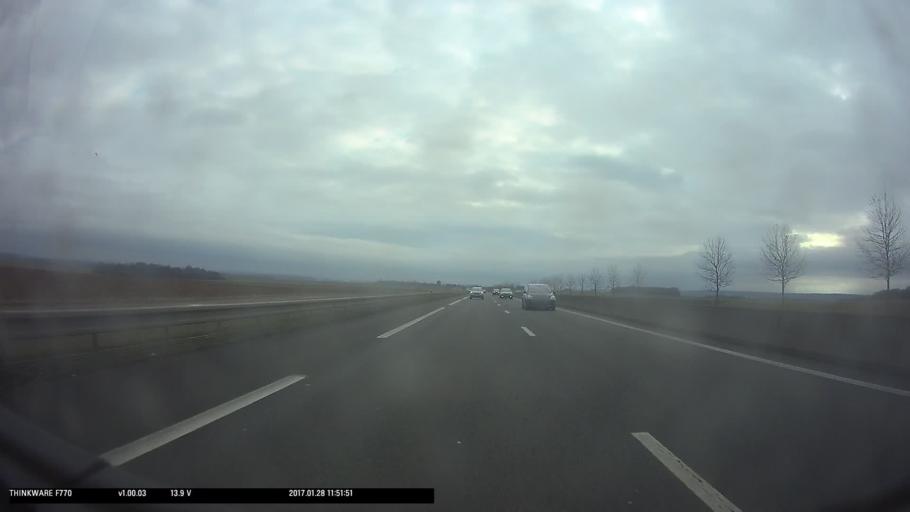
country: FR
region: Ile-de-France
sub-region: Departement du Val-d'Oise
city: Vigny
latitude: 49.0808
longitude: 1.9366
